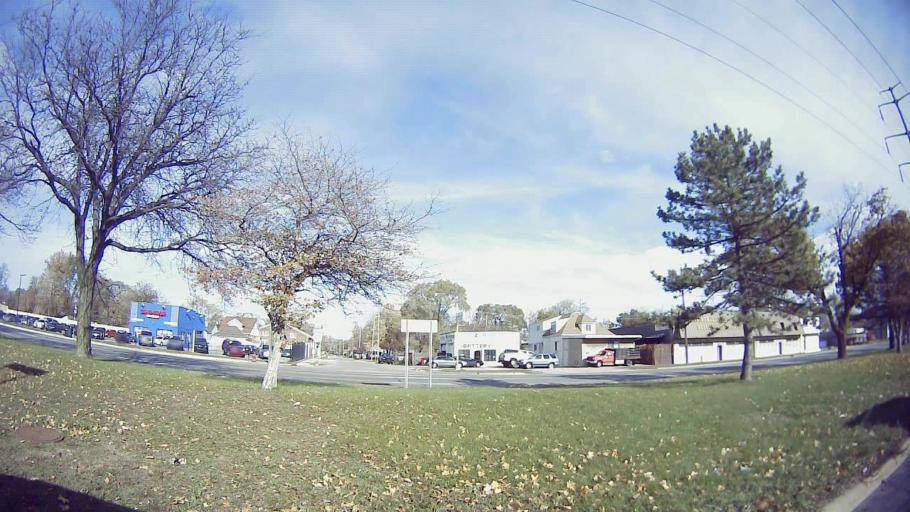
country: US
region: Michigan
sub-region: Macomb County
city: Warren
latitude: 42.4481
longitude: -83.0314
